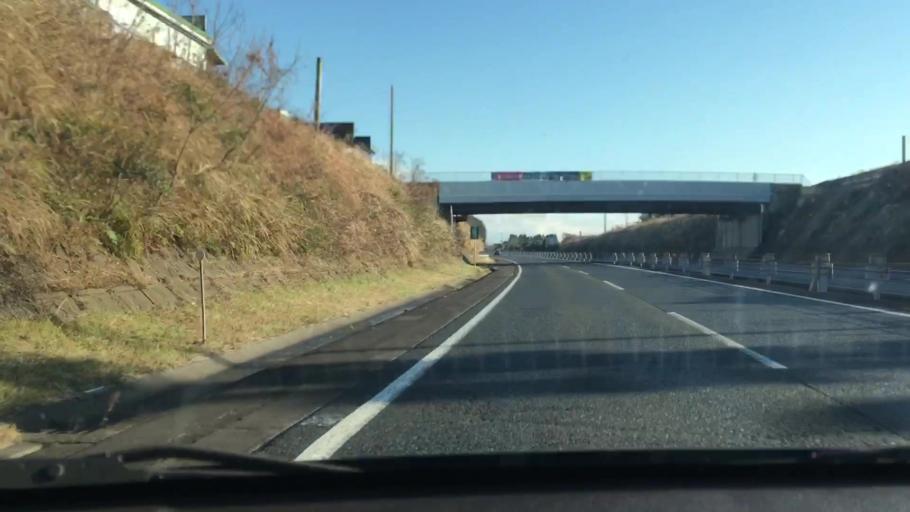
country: JP
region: Kagoshima
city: Kajiki
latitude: 31.8051
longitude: 130.7094
